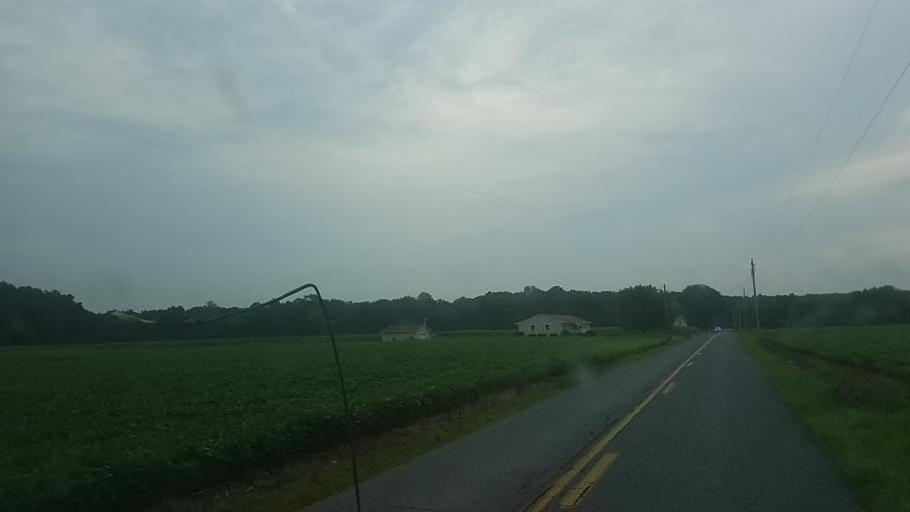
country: US
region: Delaware
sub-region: Sussex County
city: Selbyville
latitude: 38.4439
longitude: -75.2068
